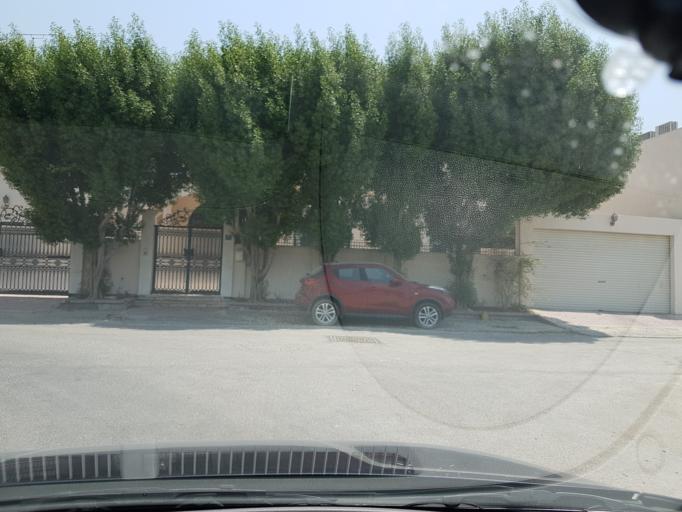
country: BH
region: Manama
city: Manama
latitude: 26.2078
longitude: 50.5707
